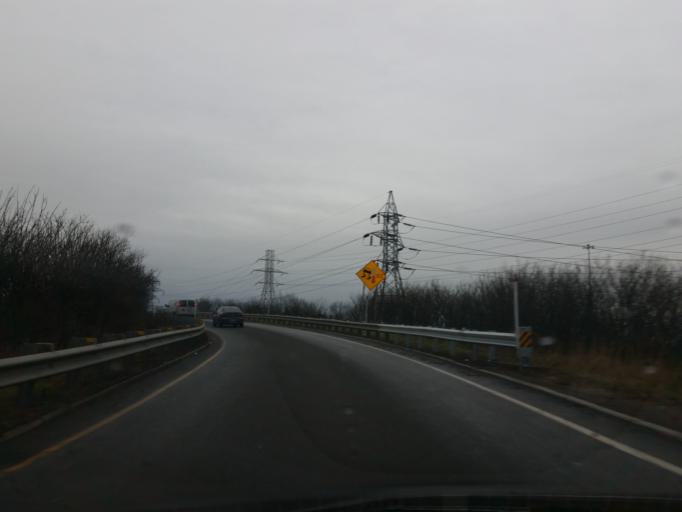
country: CA
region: Quebec
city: Quebec
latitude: 46.8348
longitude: -71.2643
